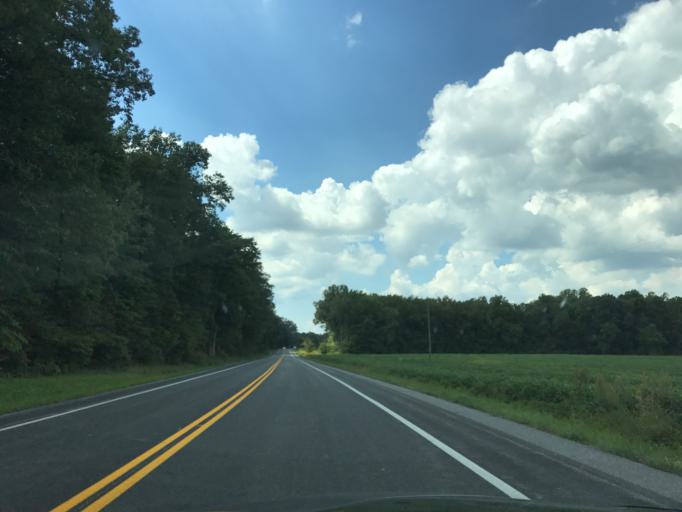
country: US
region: Maryland
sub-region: Queen Anne's County
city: Kingstown
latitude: 39.1414
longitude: -75.9173
